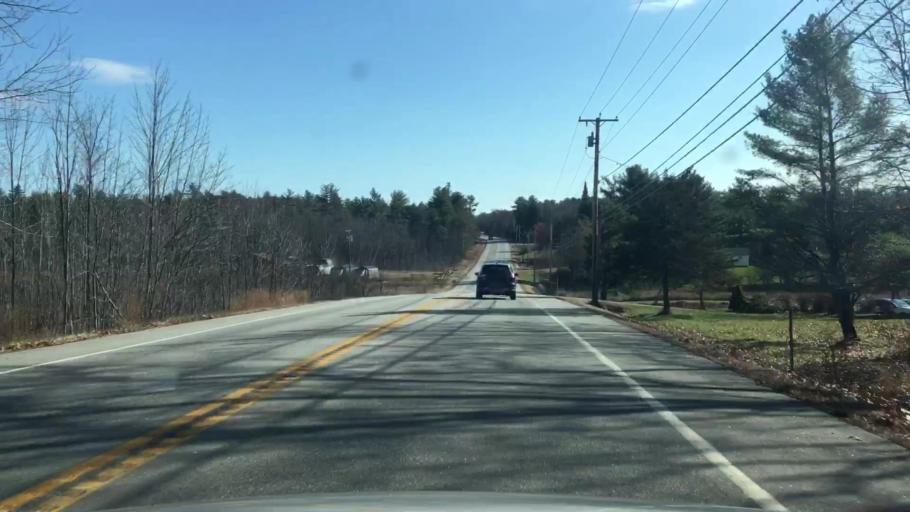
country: US
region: Maine
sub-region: Kennebec County
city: Chelsea
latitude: 44.2841
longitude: -69.6957
